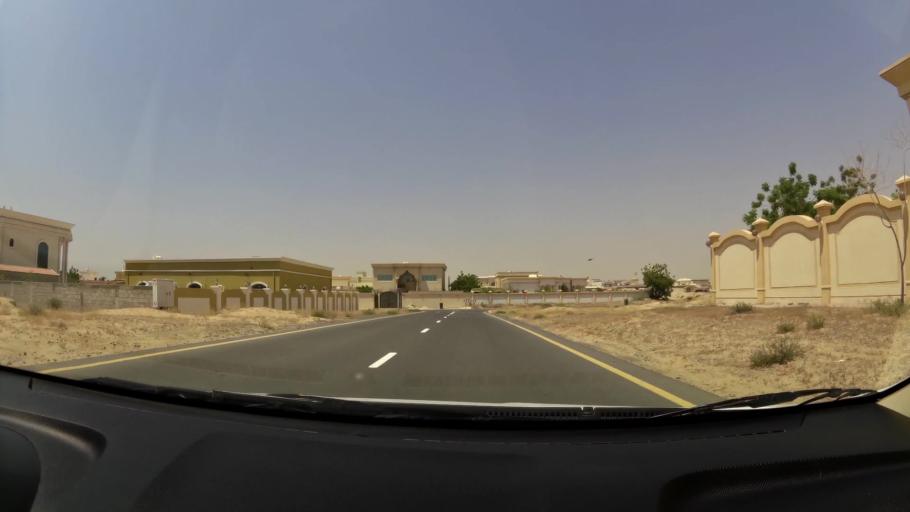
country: AE
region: Ajman
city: Ajman
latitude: 25.4240
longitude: 55.5150
